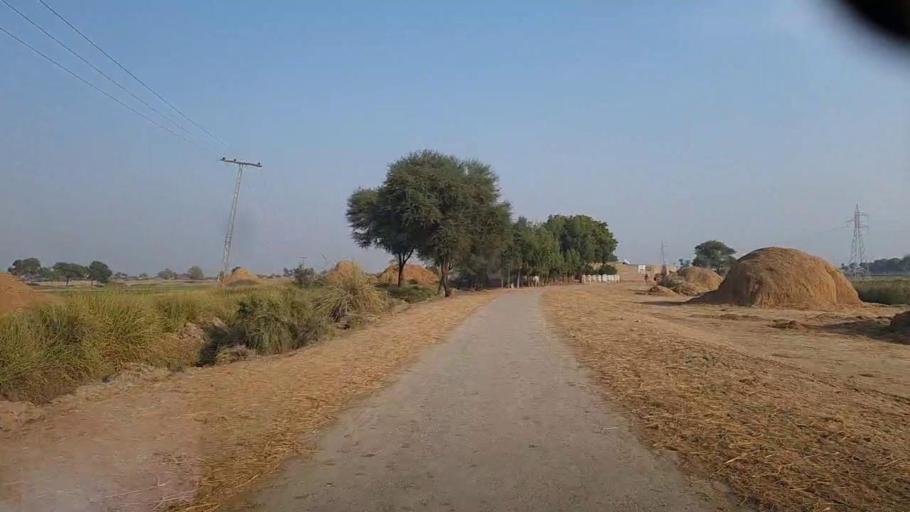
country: PK
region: Sindh
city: Jacobabad
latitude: 28.2407
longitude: 68.4992
